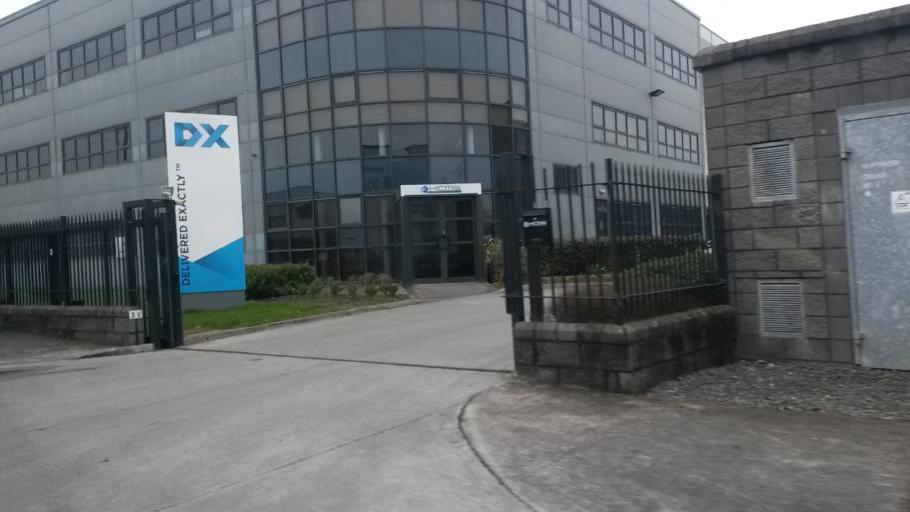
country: IE
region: Leinster
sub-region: Dublin City
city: Finglas
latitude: 53.3970
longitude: -6.3170
